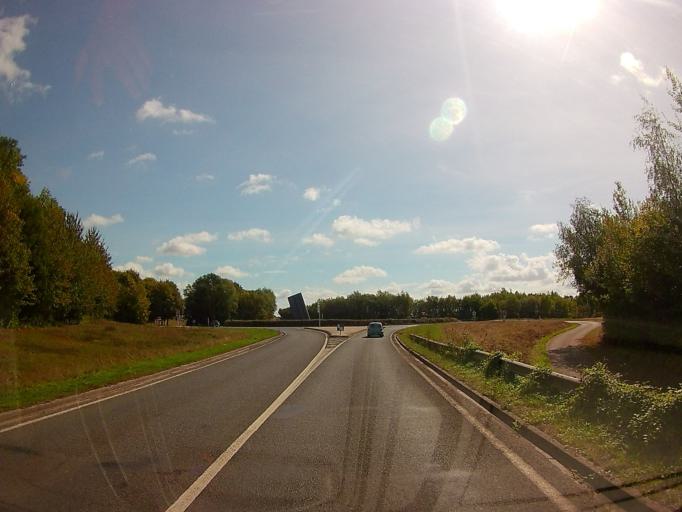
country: FR
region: Picardie
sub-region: Departement de la Somme
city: Peronne
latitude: 49.9606
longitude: 2.8598
